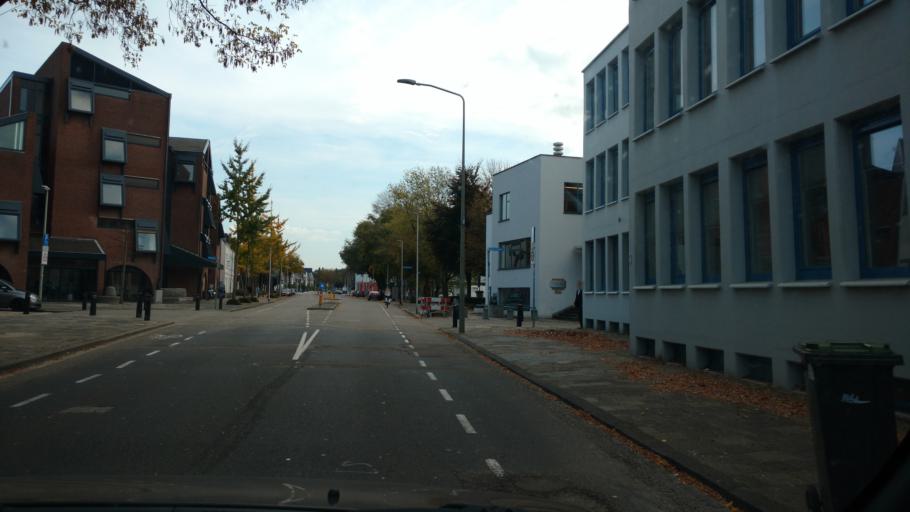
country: NL
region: Limburg
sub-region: Gemeente Heerlen
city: Heerlen
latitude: 50.8834
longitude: 5.9781
